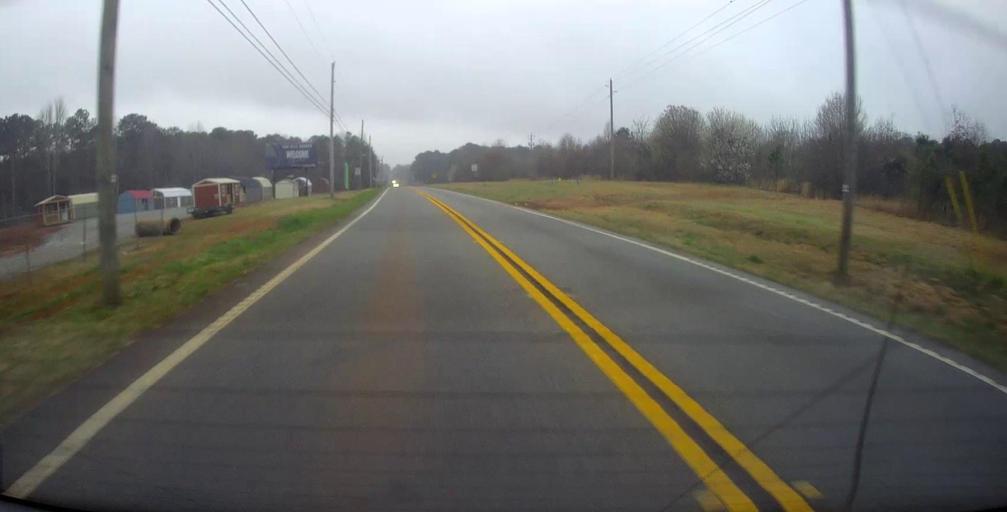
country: US
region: Georgia
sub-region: Spalding County
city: Experiment
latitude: 33.2205
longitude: -84.3111
